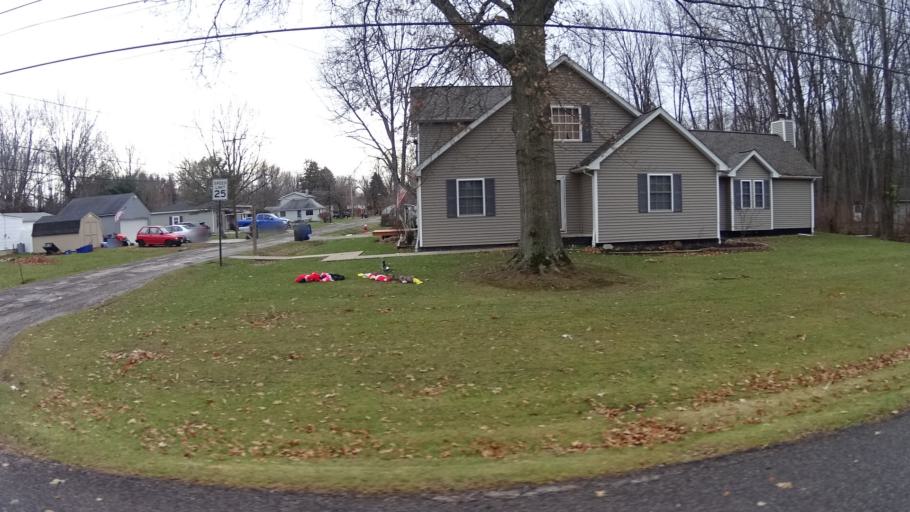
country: US
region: Ohio
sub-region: Lorain County
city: North Ridgeville
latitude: 41.3636
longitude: -82.0219
